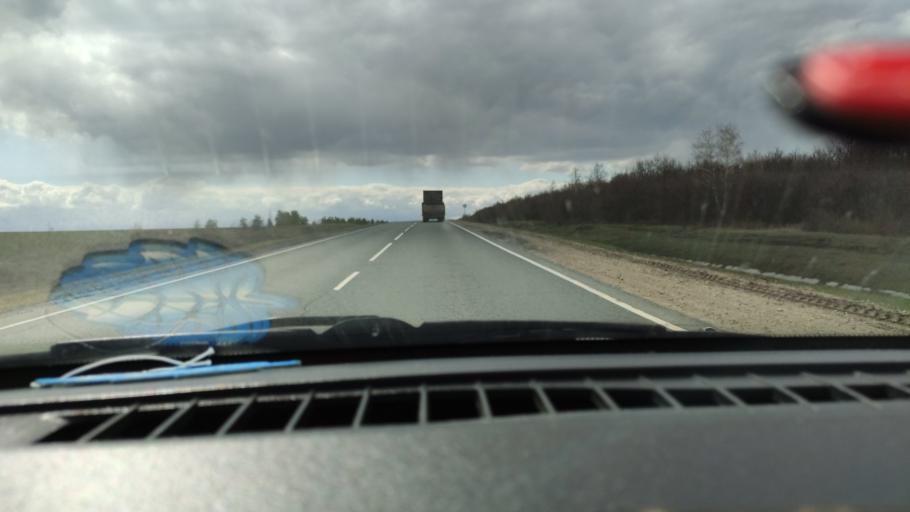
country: RU
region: Saratov
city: Alekseyevka
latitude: 52.2357
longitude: 47.9045
